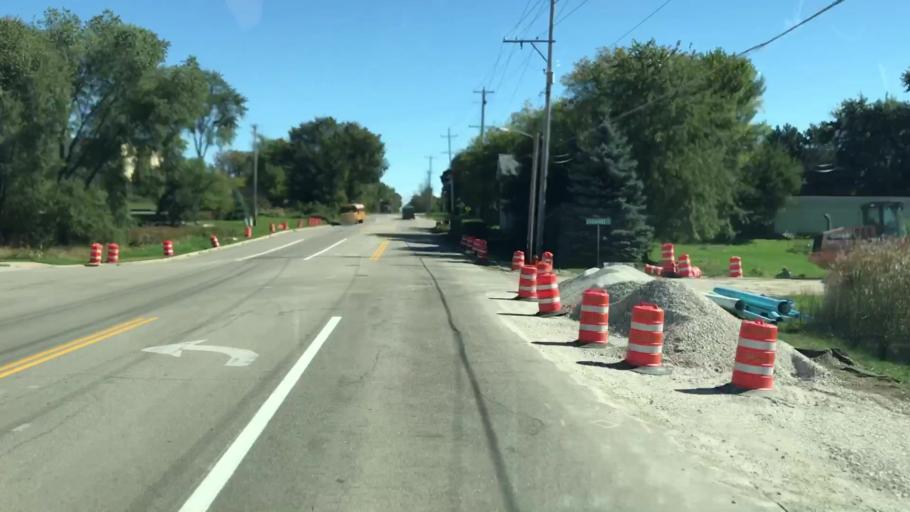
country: US
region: Wisconsin
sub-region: Waukesha County
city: Lannon
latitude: 43.1046
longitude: -88.1394
